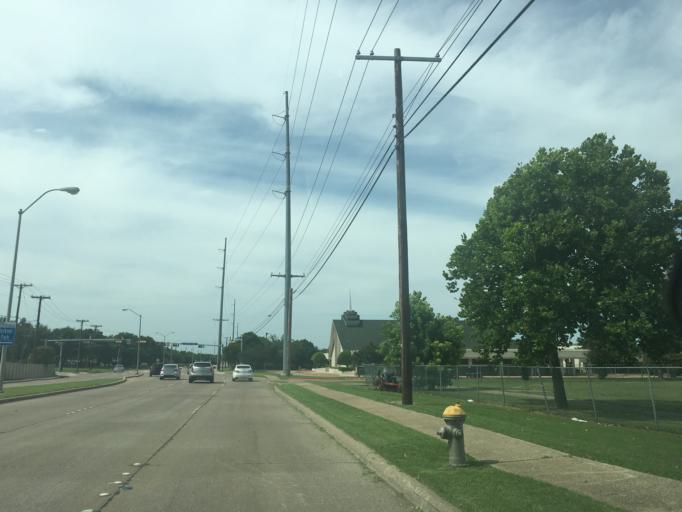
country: US
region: Texas
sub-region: Dallas County
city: Richardson
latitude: 32.9373
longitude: -96.6827
